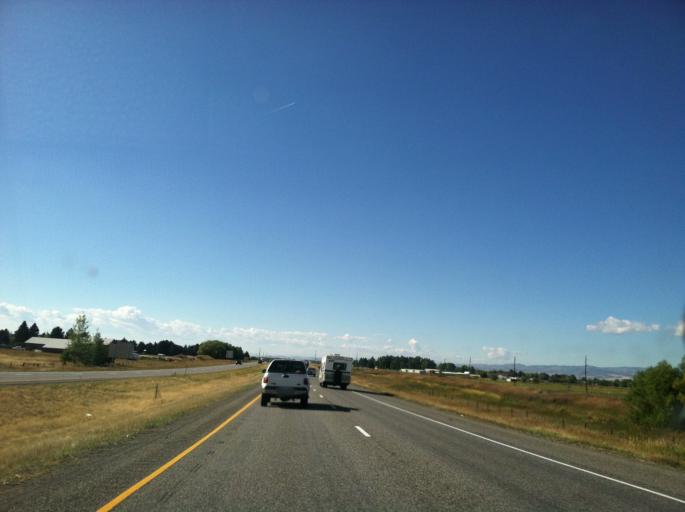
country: US
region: Montana
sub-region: Gallatin County
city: Bozeman
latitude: 45.7321
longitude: -111.0946
